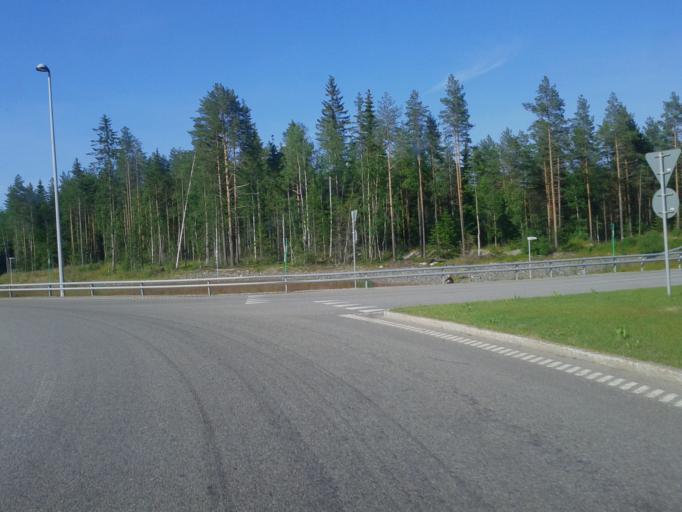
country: SE
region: Vaesterbotten
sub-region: Umea Kommun
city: Umea
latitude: 63.8133
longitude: 20.3269
